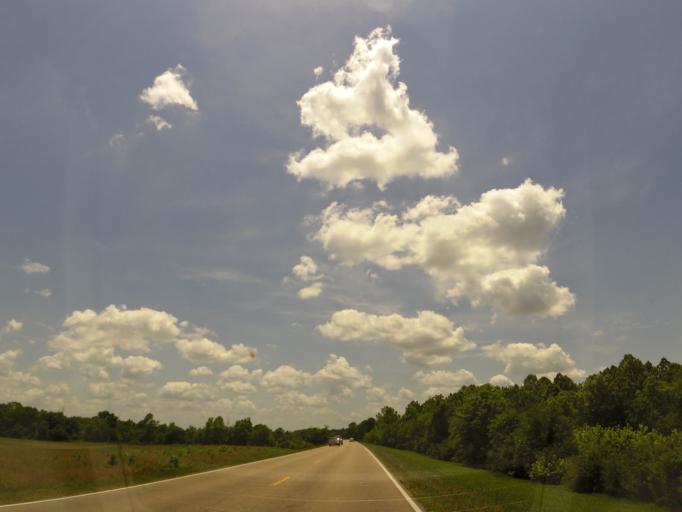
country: US
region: Mississippi
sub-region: Lee County
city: Verona
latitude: 34.2276
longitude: -88.7733
